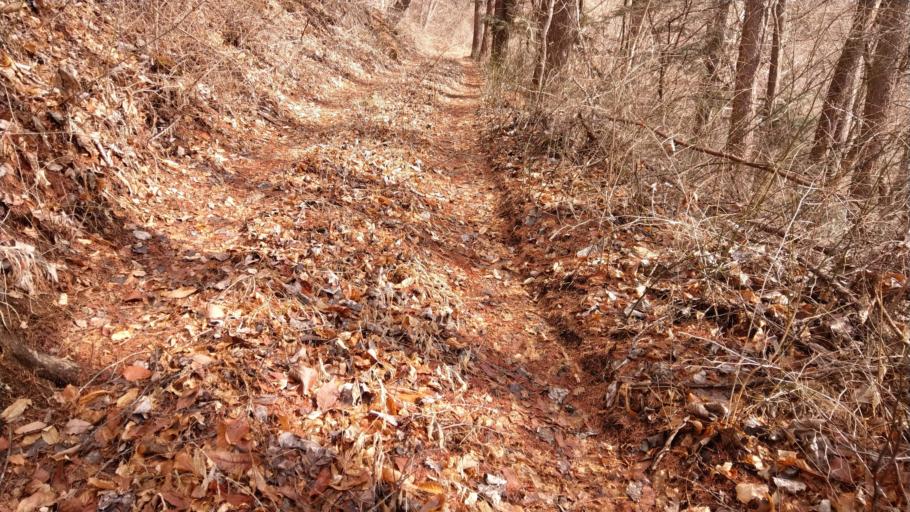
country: JP
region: Nagano
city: Komoro
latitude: 36.3711
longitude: 138.4415
